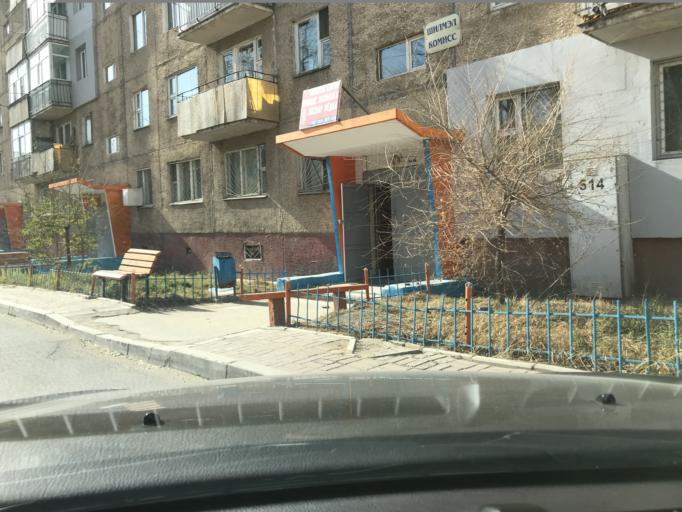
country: MN
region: Ulaanbaatar
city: Ulaanbaatar
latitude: 47.9225
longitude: 106.9439
